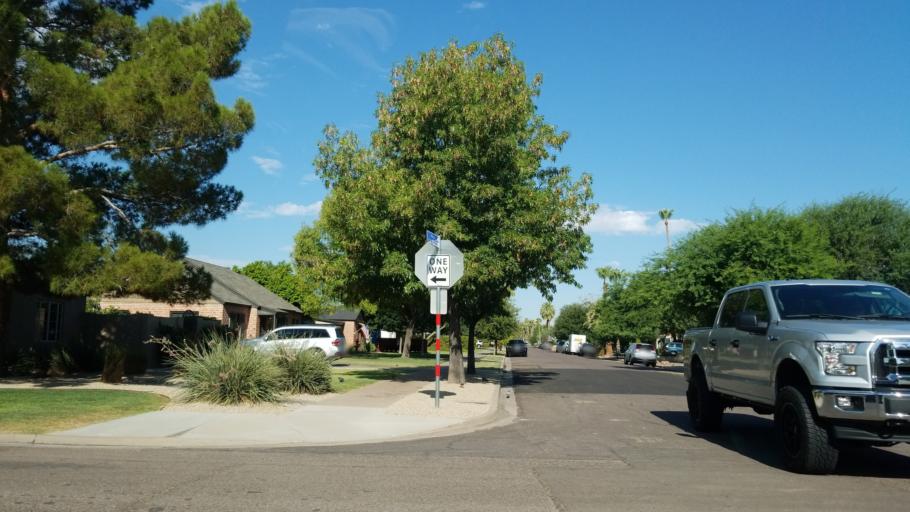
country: US
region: Arizona
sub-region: Maricopa County
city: Phoenix
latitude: 33.4740
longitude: -112.0804
